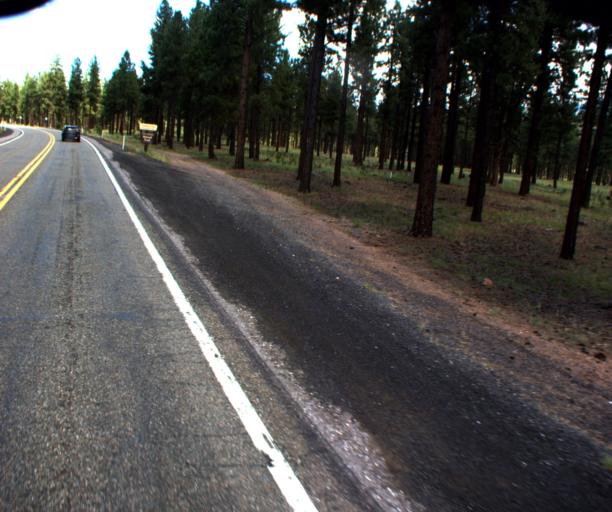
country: US
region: Arizona
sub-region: Coconino County
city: Flagstaff
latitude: 35.2771
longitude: -111.7450
